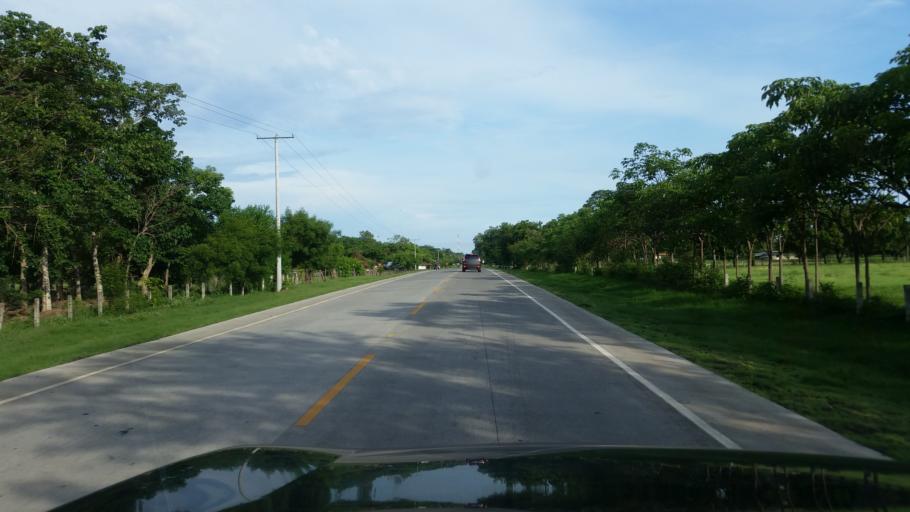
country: NI
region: Managua
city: Carlos Fonseca Amador
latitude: 12.0799
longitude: -86.5140
